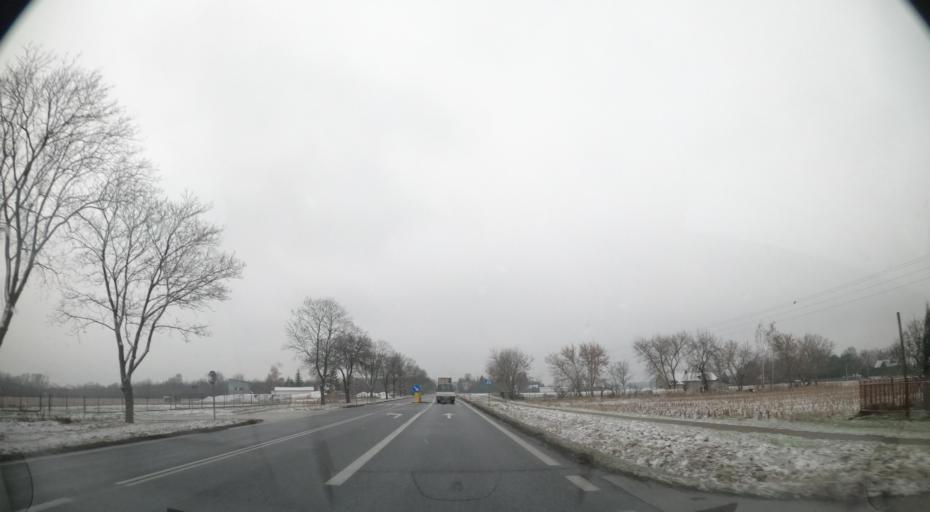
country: PL
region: Masovian Voivodeship
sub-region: Powiat sochaczewski
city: Paprotnia
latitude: 52.2088
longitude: 20.4650
